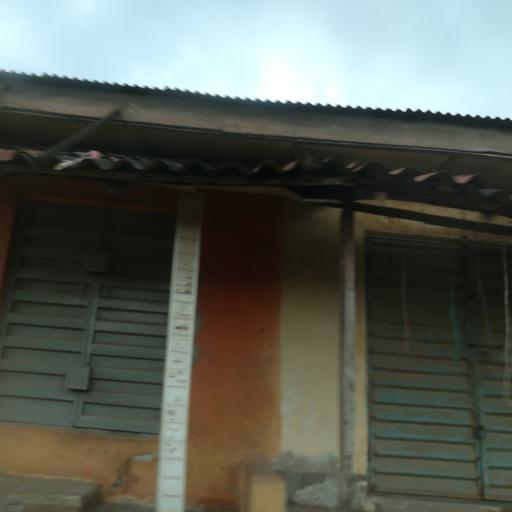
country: NG
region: Lagos
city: Agege
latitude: 6.5954
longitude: 3.3011
